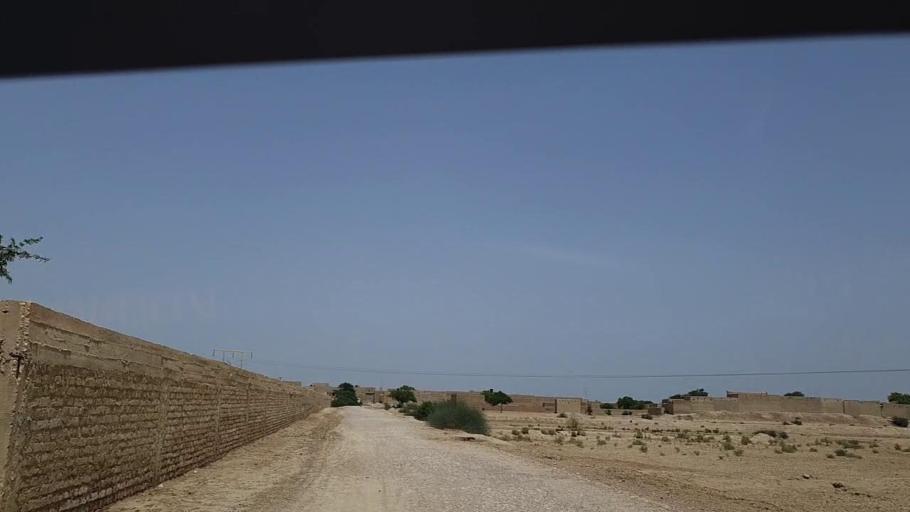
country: PK
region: Sindh
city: Johi
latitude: 26.7156
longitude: 67.6490
